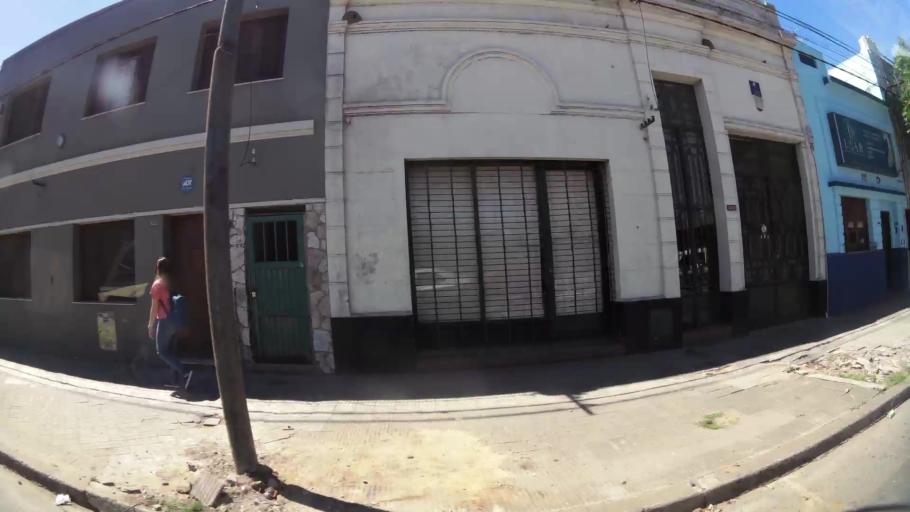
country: AR
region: Santa Fe
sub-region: Departamento de Rosario
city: Rosario
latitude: -32.9395
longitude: -60.6689
